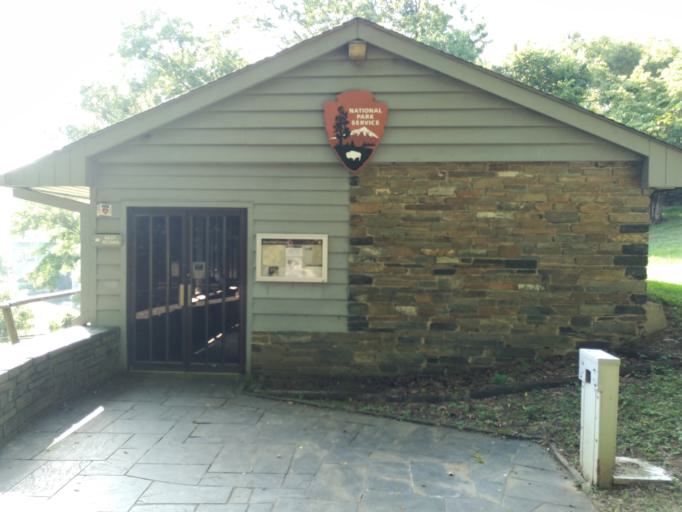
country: US
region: Virginia
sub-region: Rockbridge County
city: Glasgow
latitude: 37.5551
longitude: -79.3658
